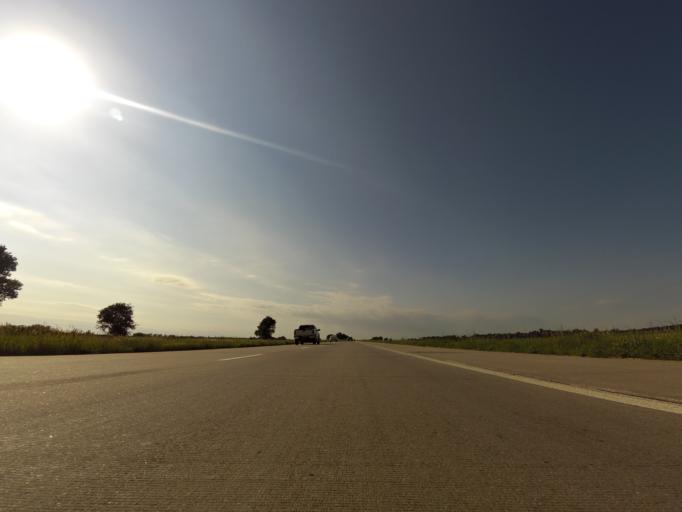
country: US
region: Kansas
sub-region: Sedgwick County
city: Colwich
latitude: 37.8581
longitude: -97.6133
